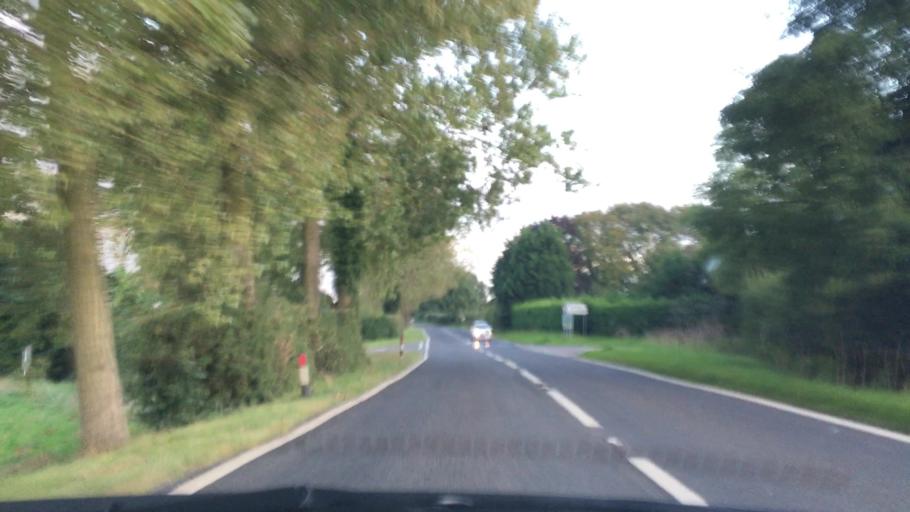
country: GB
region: England
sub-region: North East Lincolnshire
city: Wold Newton
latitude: 53.4659
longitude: -0.1034
